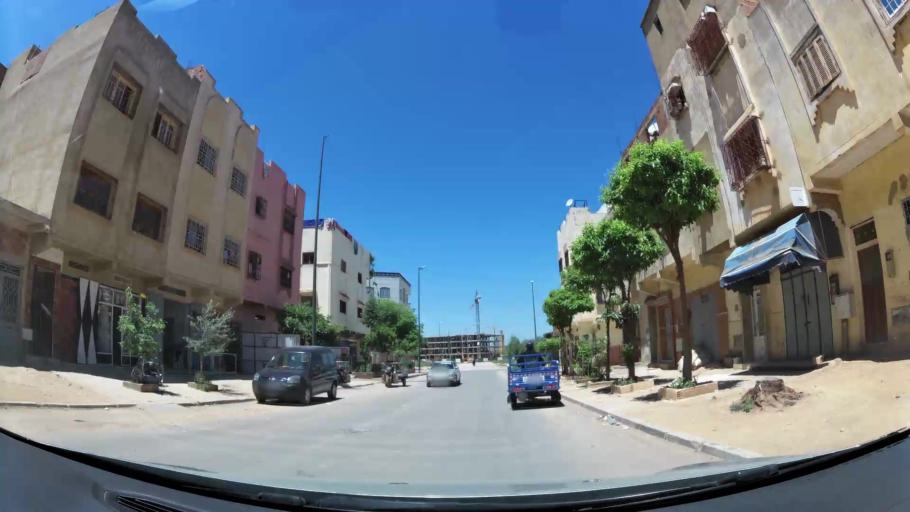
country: MA
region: Meknes-Tafilalet
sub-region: Meknes
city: Meknes
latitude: 33.8671
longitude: -5.5661
